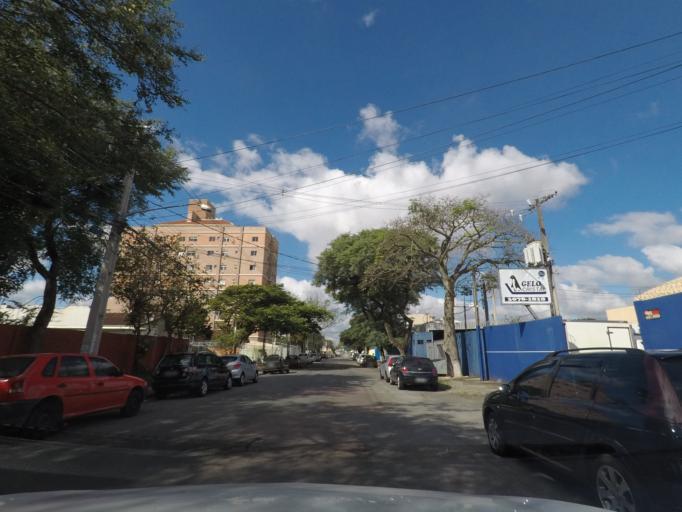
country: BR
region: Parana
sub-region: Curitiba
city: Curitiba
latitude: -25.4539
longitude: -49.2537
